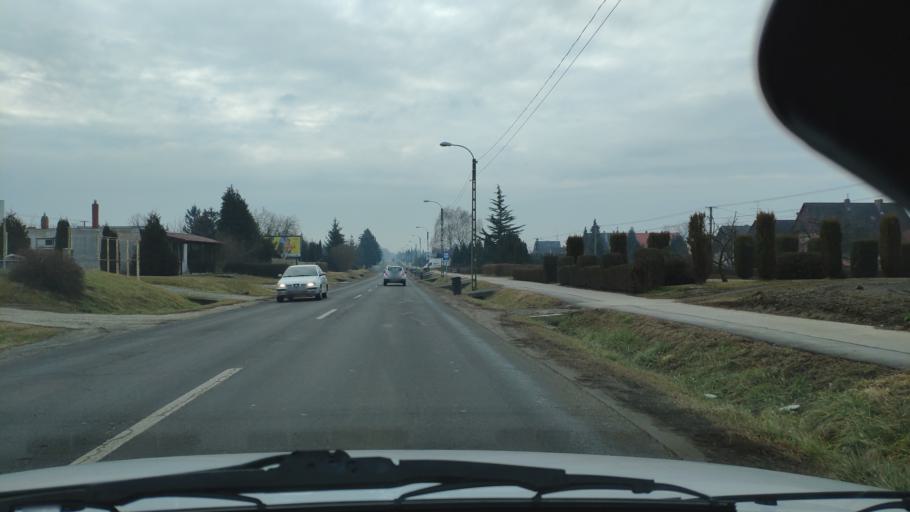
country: HU
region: Zala
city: Nagykanizsa
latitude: 46.4917
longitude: 16.9846
